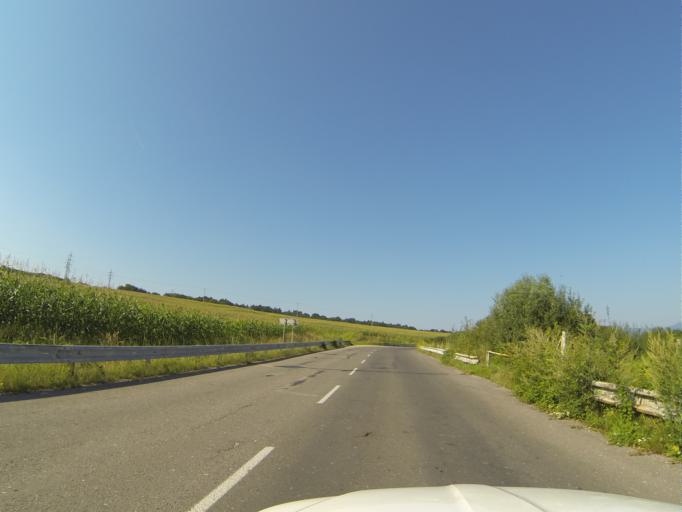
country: SK
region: Nitriansky
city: Prievidza
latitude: 48.7667
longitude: 18.6481
